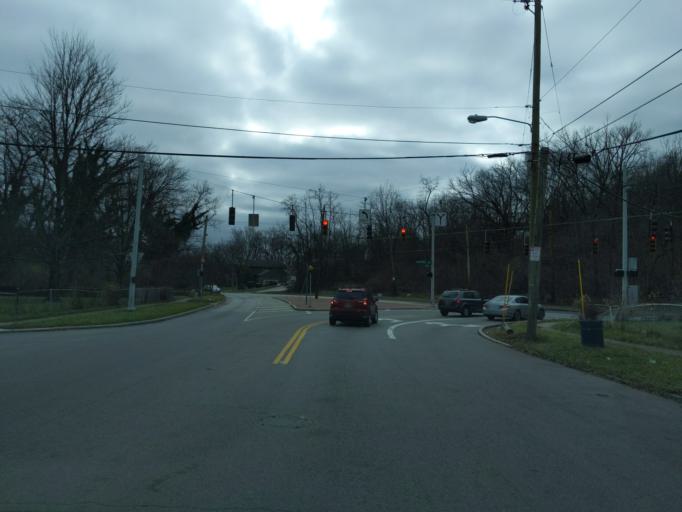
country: US
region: Ohio
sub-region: Hamilton County
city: Finneytown
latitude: 39.1745
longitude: -84.5476
